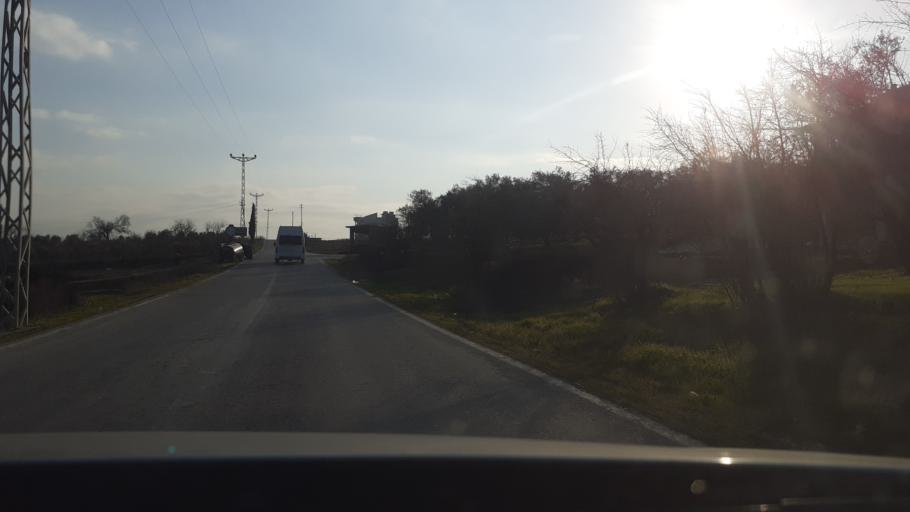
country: TR
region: Hatay
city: Boynuyogun
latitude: 36.1372
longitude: 36.3137
